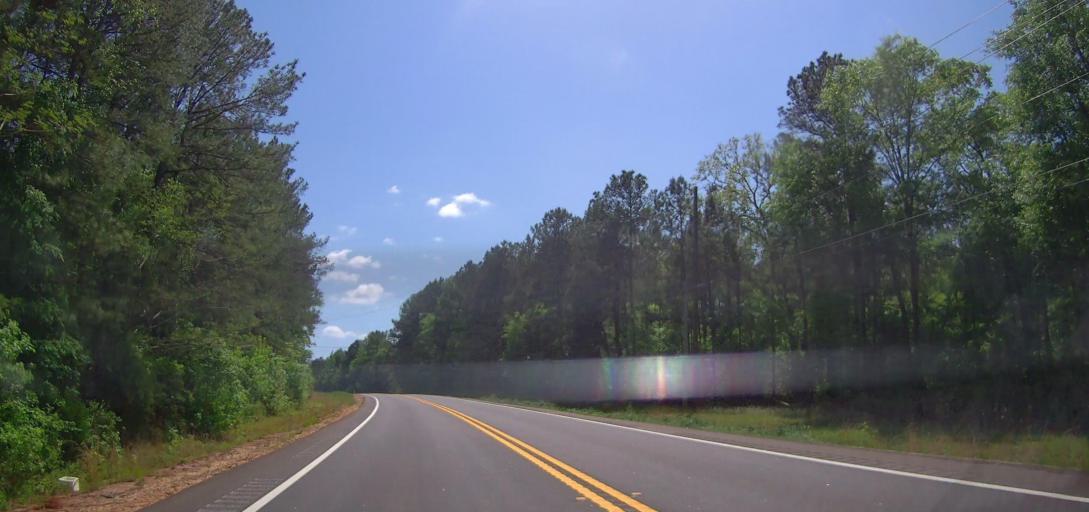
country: US
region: Georgia
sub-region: Putnam County
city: Eatonton
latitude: 33.2104
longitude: -83.4345
